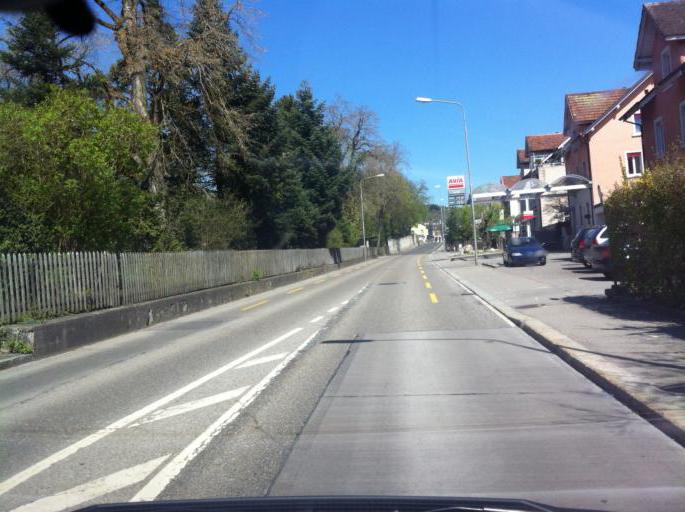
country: CH
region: Schaffhausen
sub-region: Bezirk Schaffhausen
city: Schaffhausen
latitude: 47.7043
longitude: 8.6274
